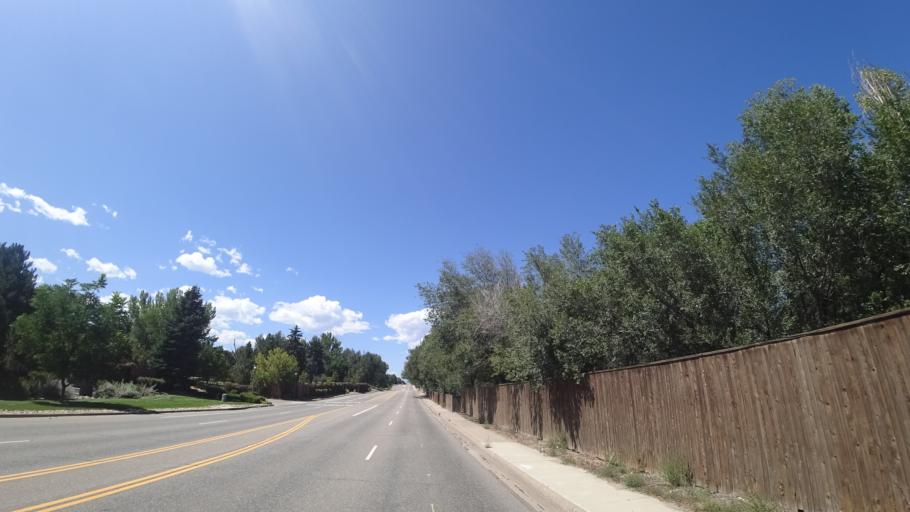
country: US
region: Colorado
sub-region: Arapahoe County
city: Greenwood Village
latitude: 39.6244
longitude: -104.9639
